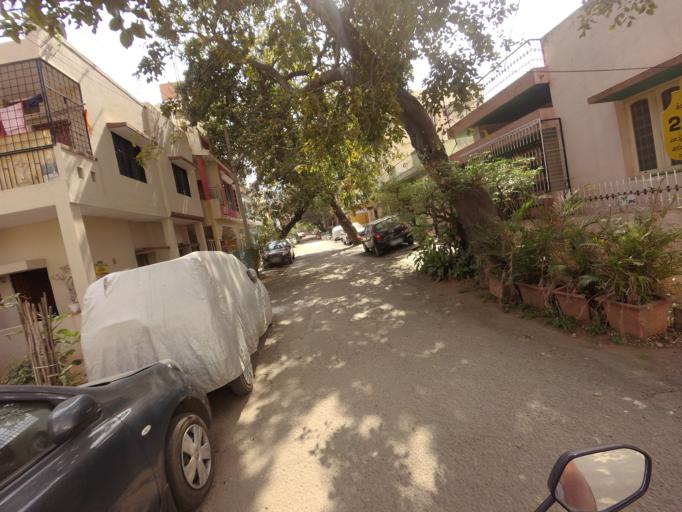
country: IN
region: Karnataka
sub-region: Bangalore Urban
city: Bangalore
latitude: 12.9633
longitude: 77.5371
